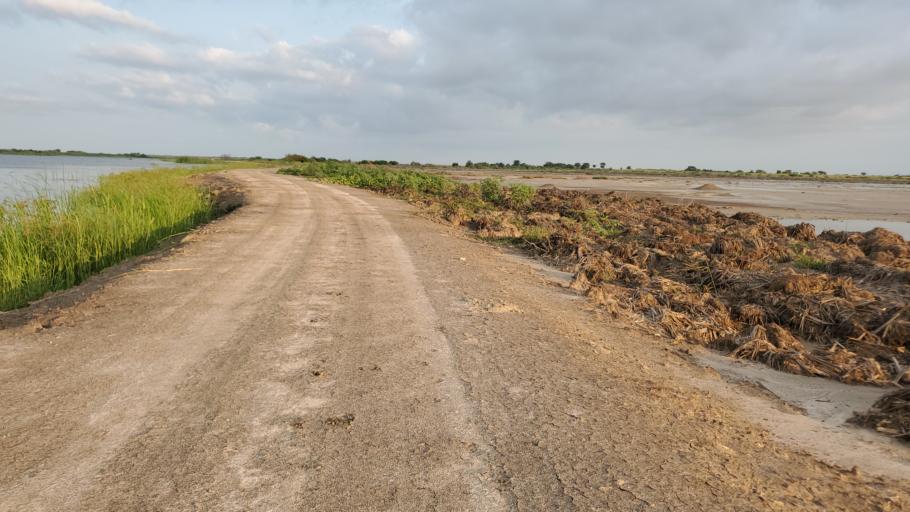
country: SN
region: Saint-Louis
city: Saint-Louis
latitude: 16.0199
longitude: -16.4065
